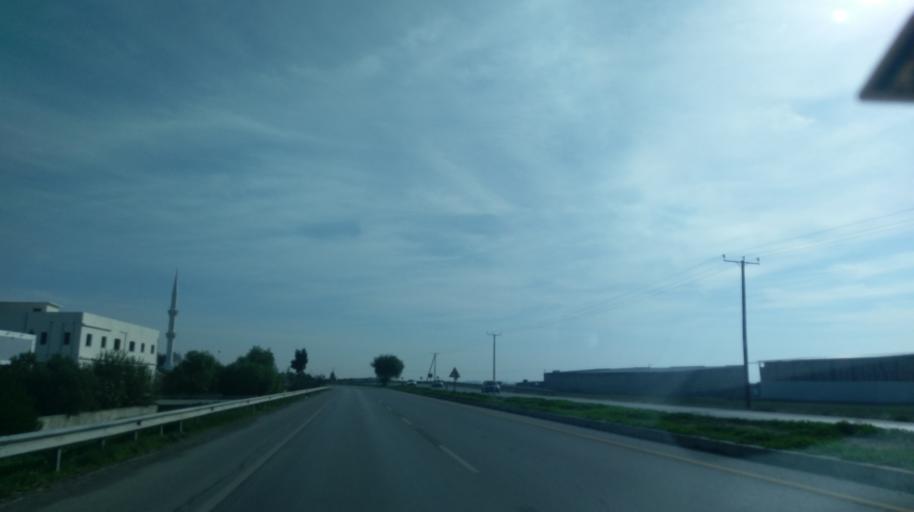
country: CY
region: Lefkosia
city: Geri
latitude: 35.2127
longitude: 33.5228
